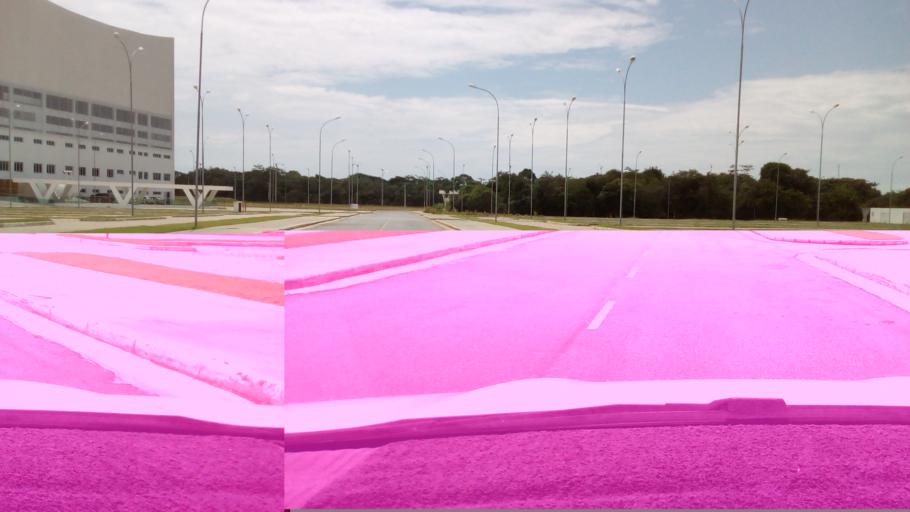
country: BR
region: Paraiba
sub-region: Joao Pessoa
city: Joao Pessoa
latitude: -7.1897
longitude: -34.8054
